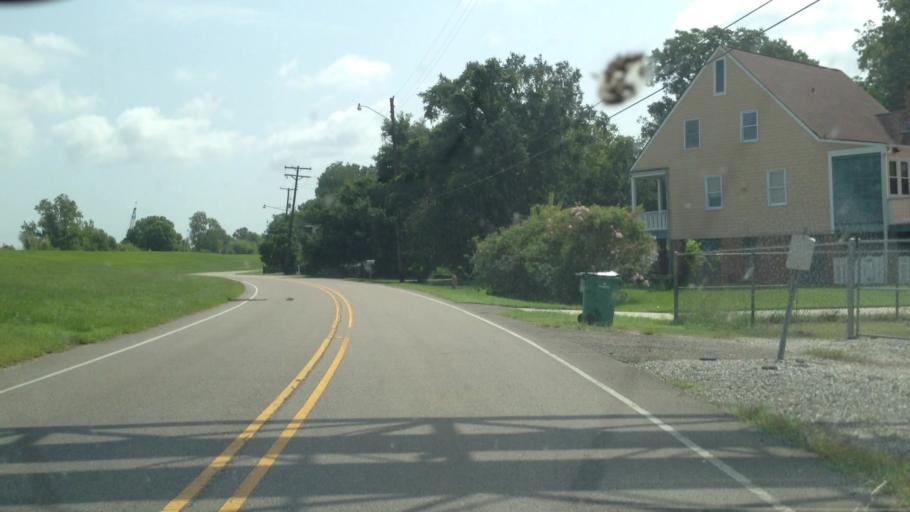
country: US
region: Louisiana
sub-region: Jefferson Parish
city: Jefferson
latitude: 29.9493
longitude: -90.1555
